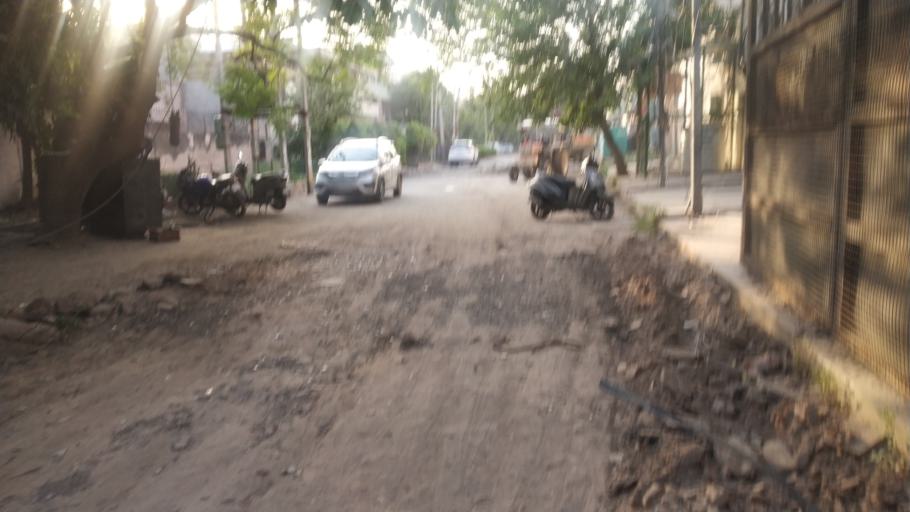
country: IN
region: Punjab
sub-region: Ajitgarh
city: Mohali
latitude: 30.7081
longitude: 76.7229
